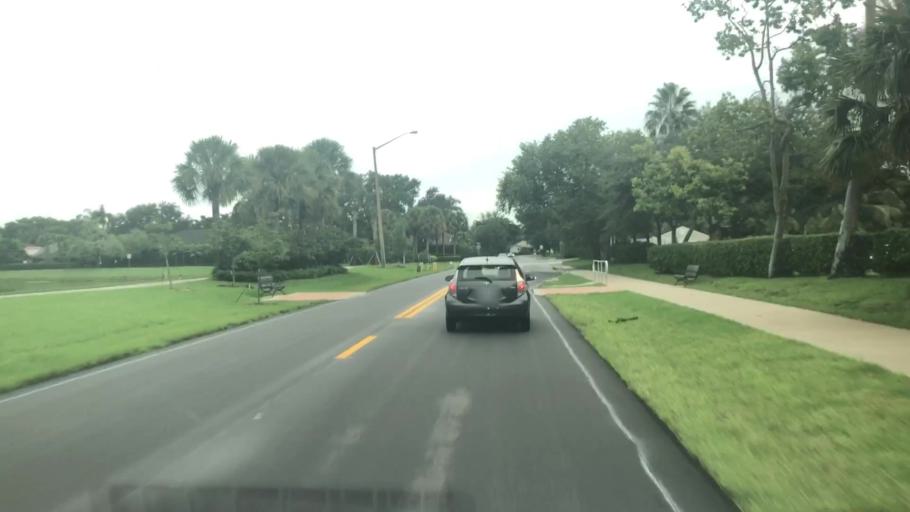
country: US
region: Florida
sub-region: Palm Beach County
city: Boca Pointe
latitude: 26.2972
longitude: -80.1847
